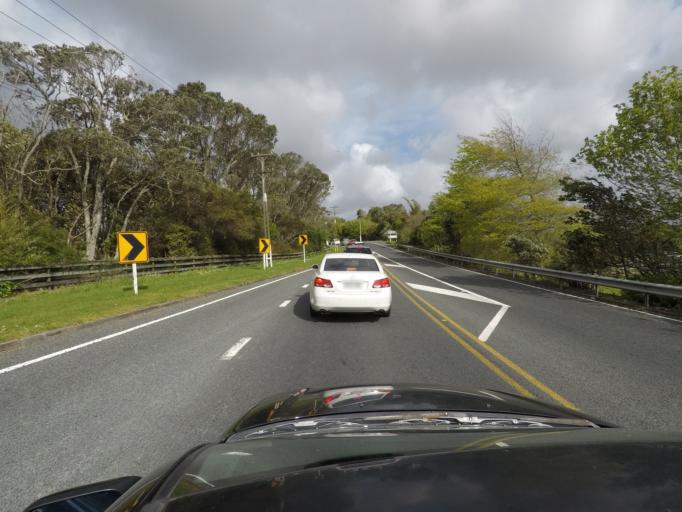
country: NZ
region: Auckland
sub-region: Auckland
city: Pakuranga
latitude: -36.9434
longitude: 174.9499
